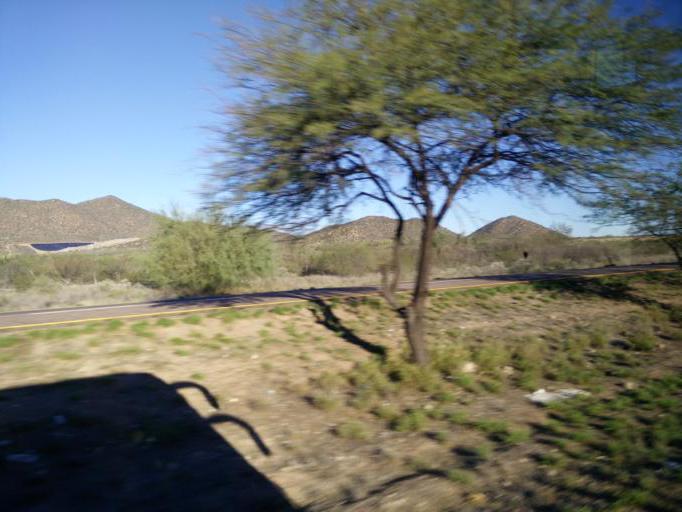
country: MX
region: Sonora
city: Heroica Guaymas
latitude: 27.9984
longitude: -110.9379
